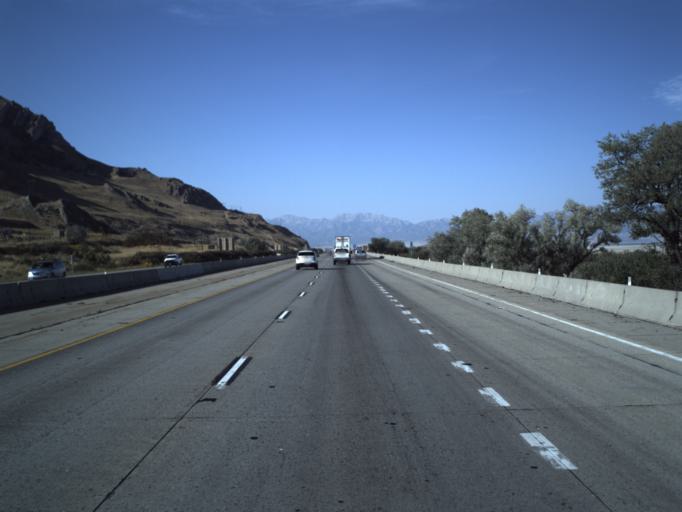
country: US
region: Utah
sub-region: Tooele County
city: Stansbury park
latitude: 40.7191
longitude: -112.2332
